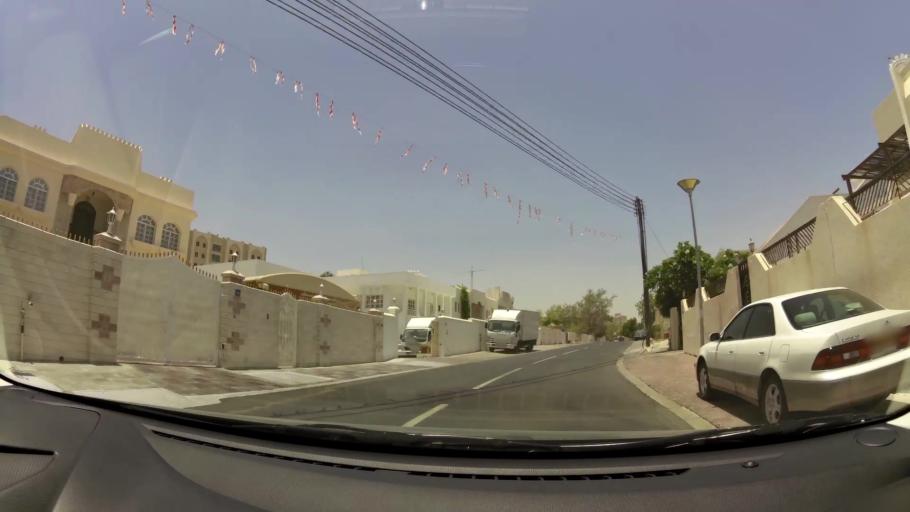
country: OM
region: Muhafazat Masqat
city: Bawshar
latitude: 23.6026
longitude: 58.4629
